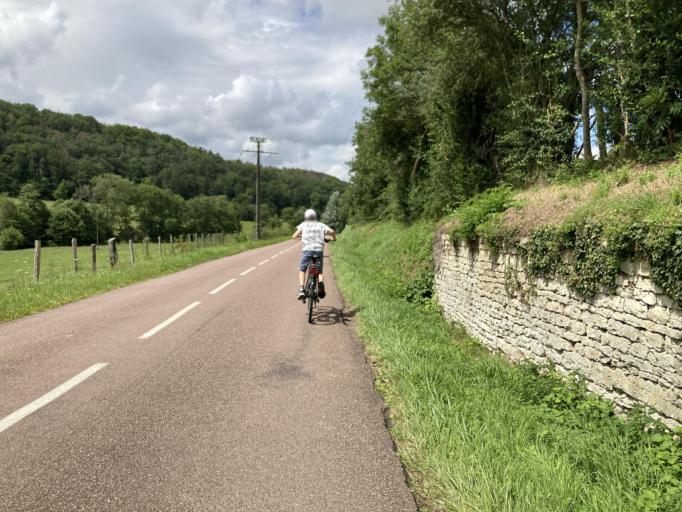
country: FR
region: Bourgogne
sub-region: Departement de la Cote-d'Or
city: Montbard
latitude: 47.6261
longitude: 4.3680
